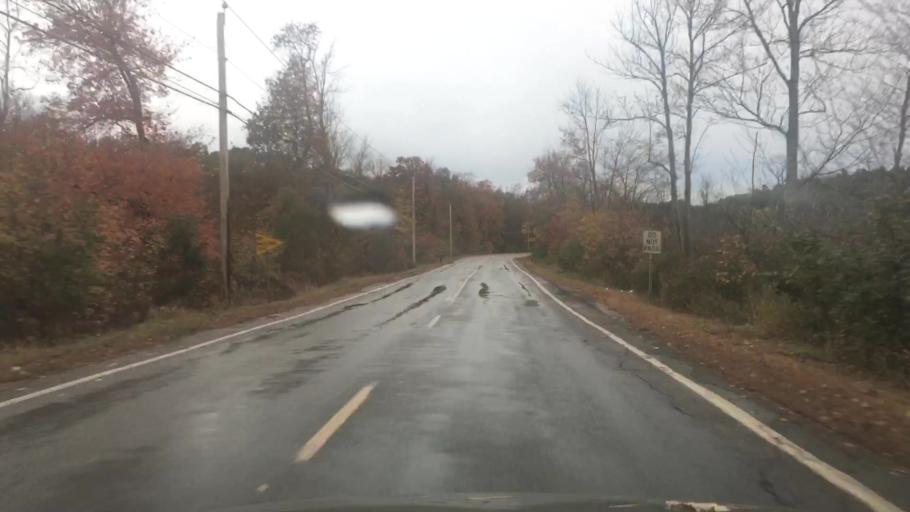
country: US
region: Connecticut
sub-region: Tolland County
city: Stafford
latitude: 41.9310
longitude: -72.1935
